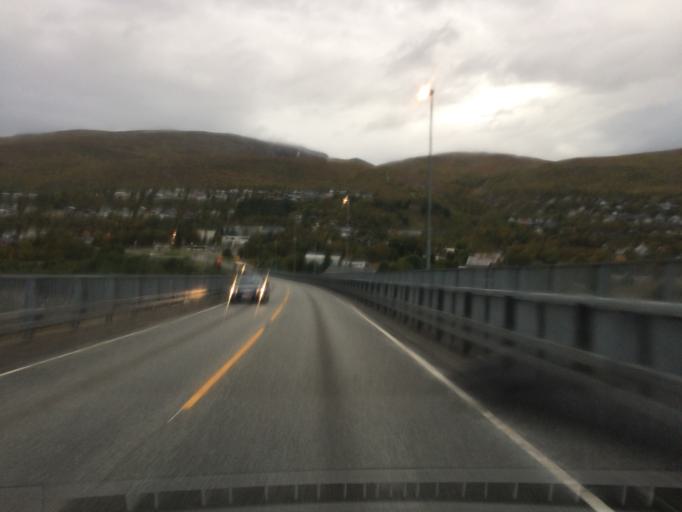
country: NO
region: Troms
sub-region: Tromso
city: Tromso
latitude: 69.6942
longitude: 18.8937
